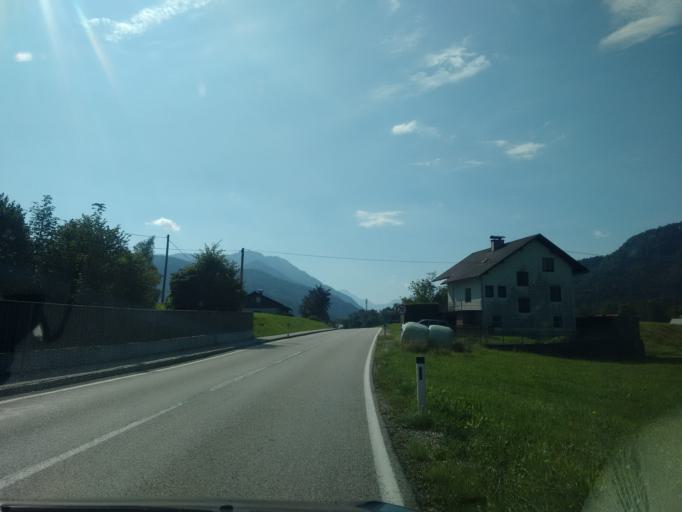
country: AT
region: Upper Austria
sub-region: Politischer Bezirk Gmunden
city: Gruenau im Almtal
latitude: 47.8648
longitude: 13.9455
